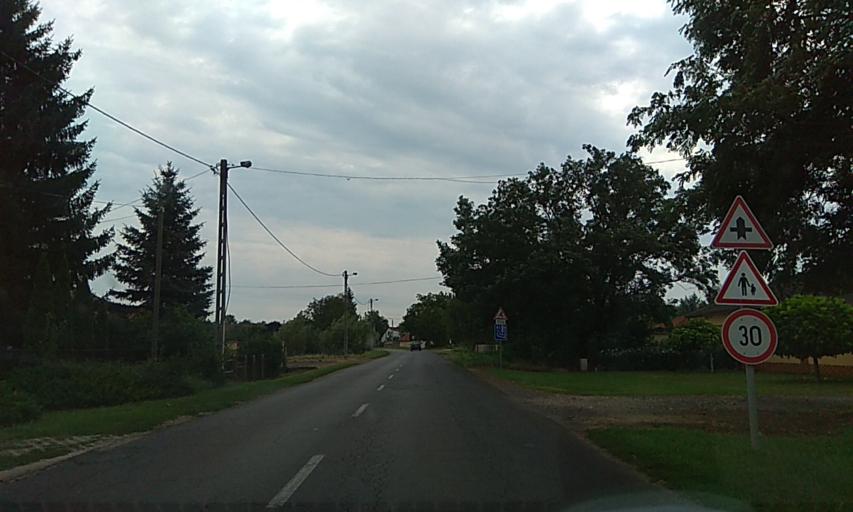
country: HU
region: Szabolcs-Szatmar-Bereg
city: Kotaj
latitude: 48.0147
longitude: 21.6877
